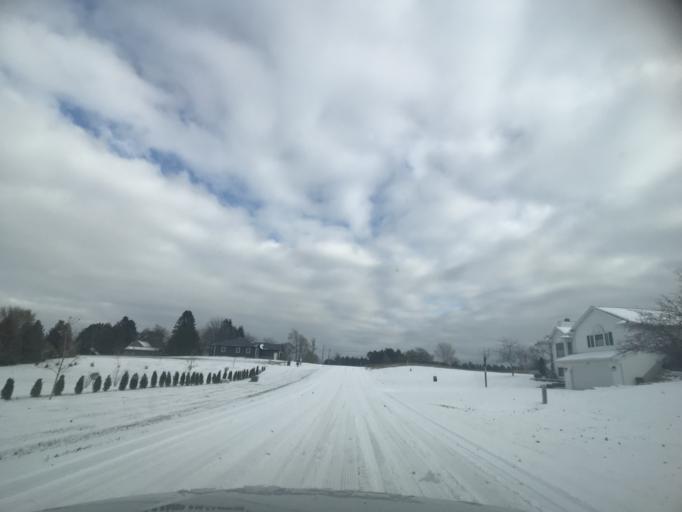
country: US
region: Wisconsin
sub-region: Door County
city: Sturgeon Bay
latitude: 44.8188
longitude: -87.3665
